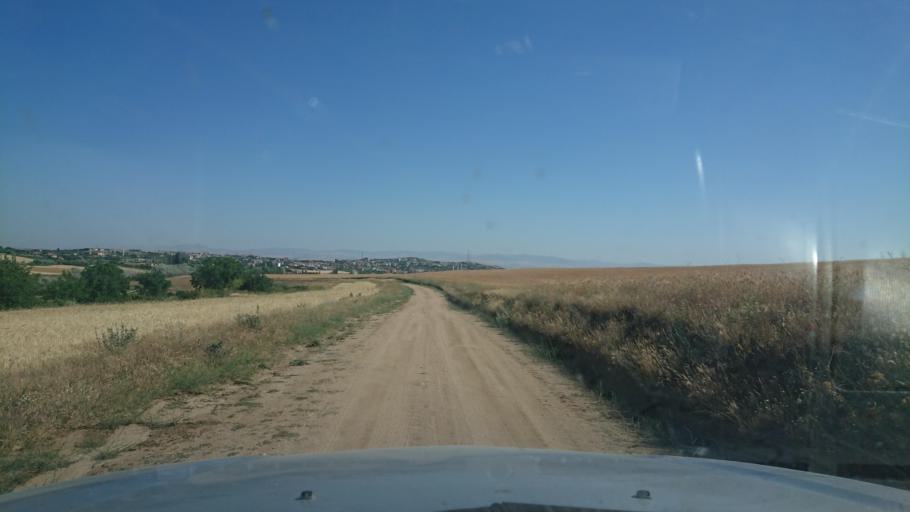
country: TR
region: Aksaray
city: Agacoren
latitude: 38.8528
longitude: 33.9145
